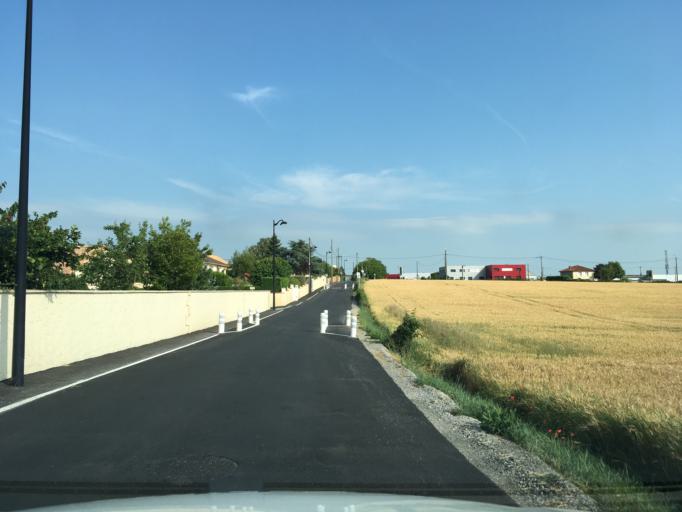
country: FR
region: Poitou-Charentes
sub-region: Departement des Deux-Sevres
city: Niort
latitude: 46.3405
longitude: -0.4226
